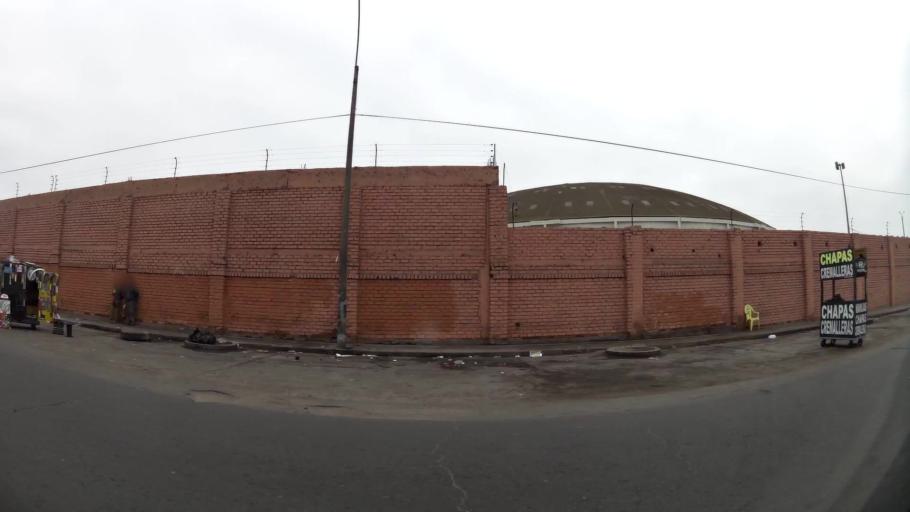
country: PE
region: Lima
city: Lima
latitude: -12.0538
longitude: -77.0626
